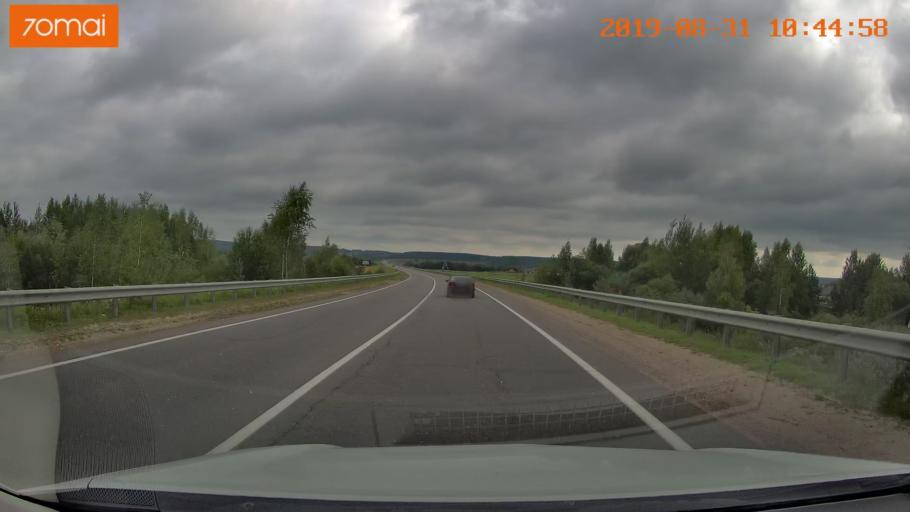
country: BY
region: Mogilev
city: Palykavichy Pyershyya
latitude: 53.9719
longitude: 30.3709
